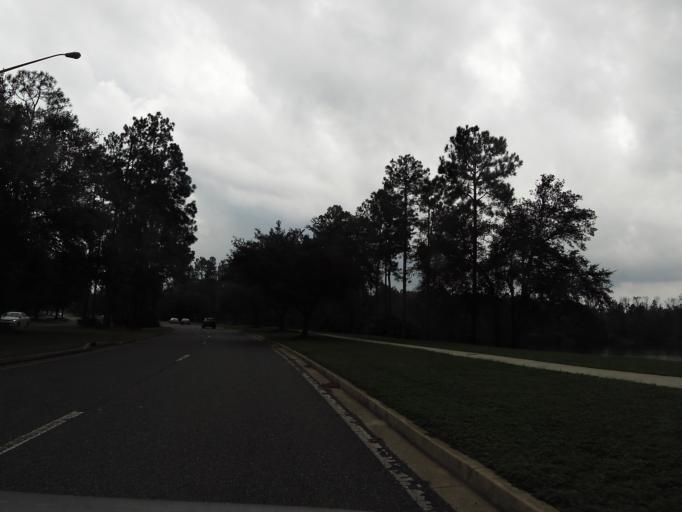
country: US
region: Florida
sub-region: Clay County
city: Lakeside
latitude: 30.1693
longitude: -81.8518
